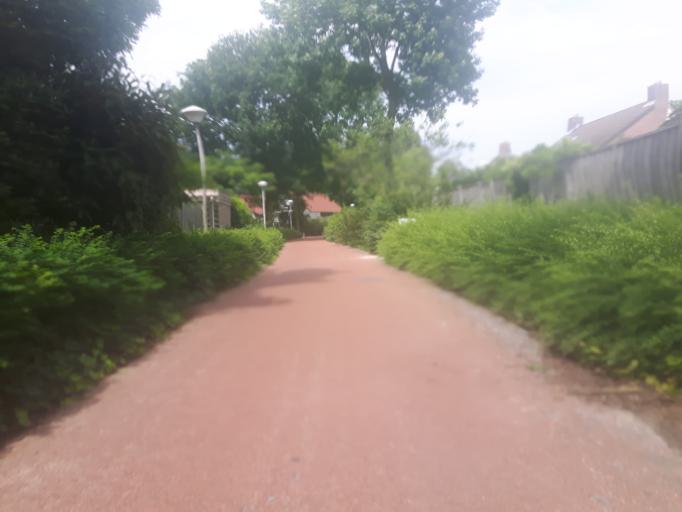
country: NL
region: Overijssel
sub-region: Gemeente Borne
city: Borne
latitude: 52.3059
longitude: 6.7599
